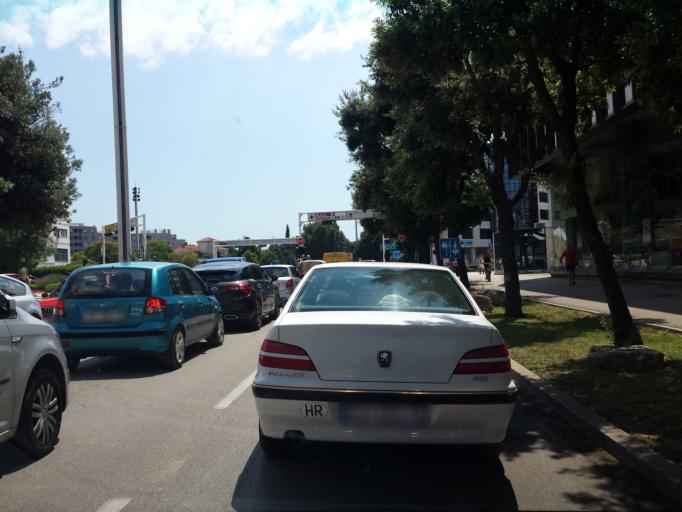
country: HR
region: Istarska
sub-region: Grad Pula
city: Pula
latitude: 44.8659
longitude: 13.8494
